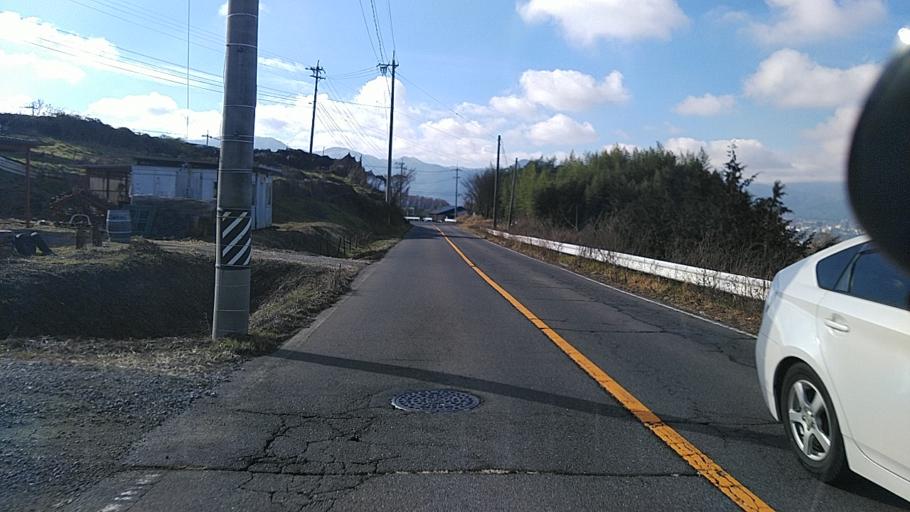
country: JP
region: Nagano
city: Shiojiri
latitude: 36.1299
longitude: 137.9857
